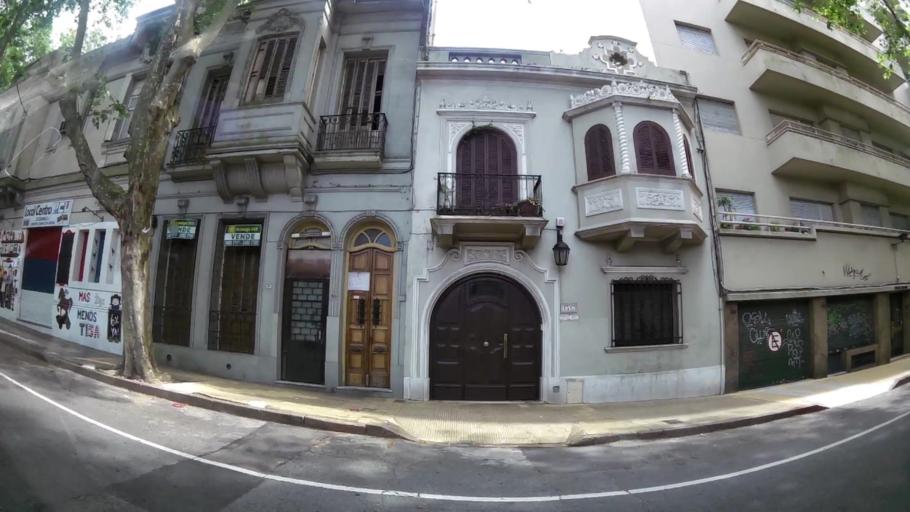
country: UY
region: Montevideo
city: Montevideo
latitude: -34.9085
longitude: -56.1873
